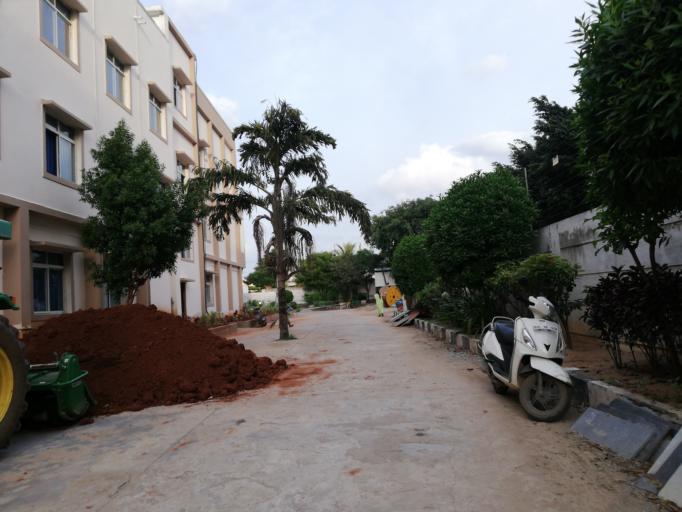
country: IN
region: Telangana
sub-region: Rangareddi
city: Quthbullapur
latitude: 17.5940
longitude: 78.4422
